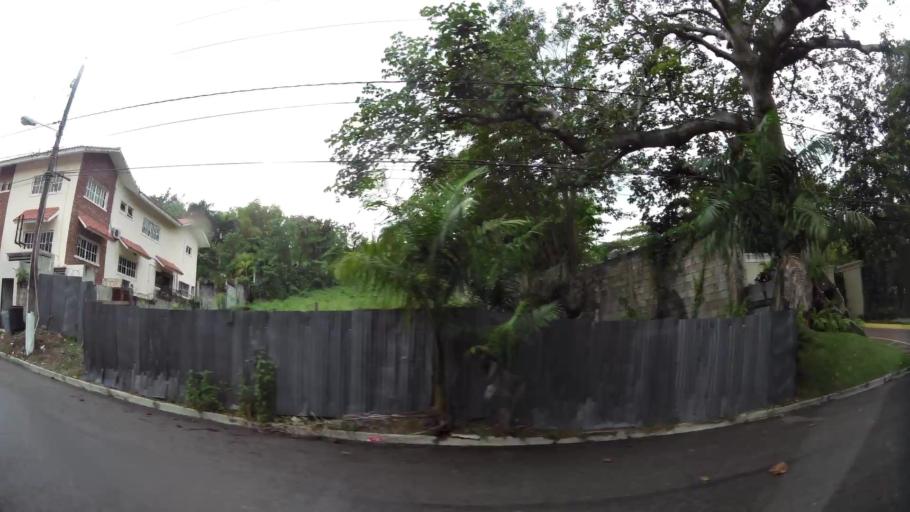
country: DO
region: Nacional
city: La Agustina
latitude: 18.5123
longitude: -69.9538
